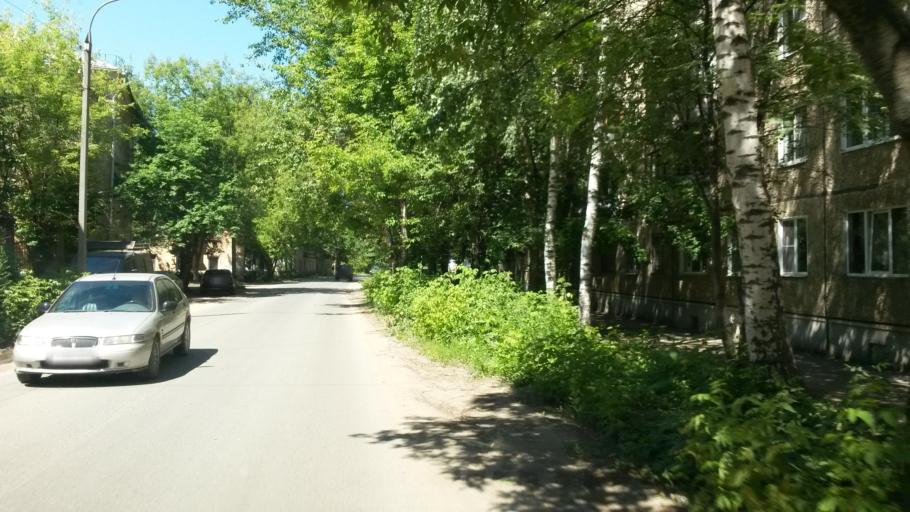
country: RU
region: Ivanovo
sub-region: Gorod Ivanovo
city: Ivanovo
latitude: 56.9816
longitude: 40.9607
